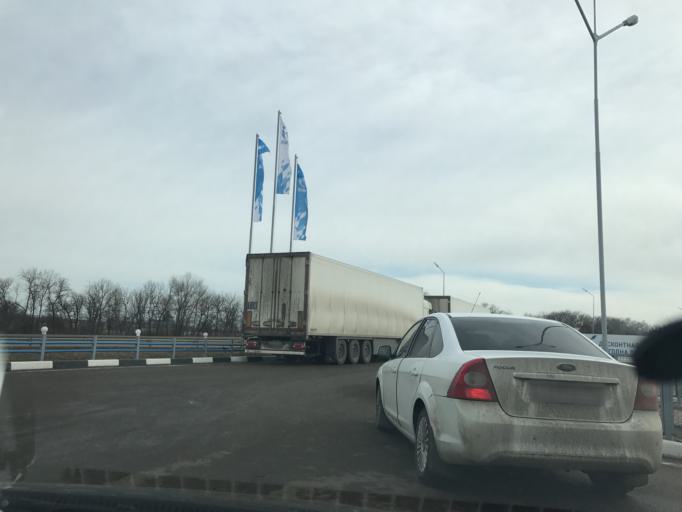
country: RU
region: Stavropol'skiy
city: Kangly
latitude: 44.2360
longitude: 43.0324
